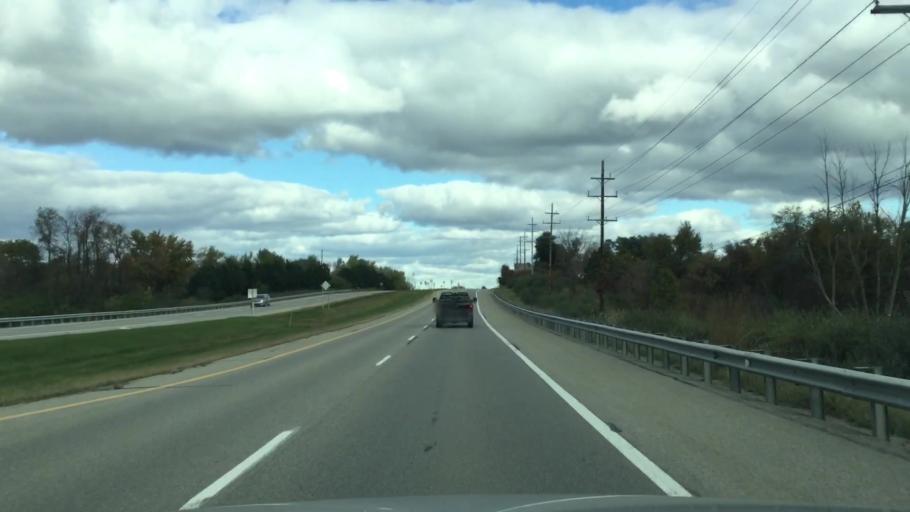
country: US
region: Michigan
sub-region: Lapeer County
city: Lapeer
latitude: 42.9658
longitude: -83.3144
